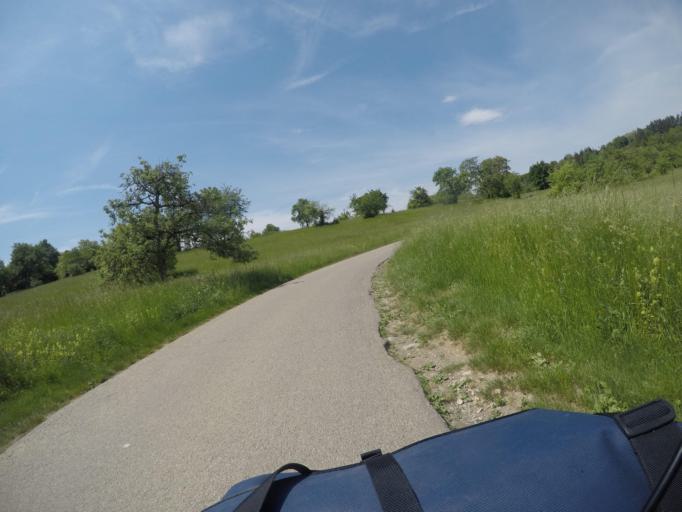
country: DE
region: Baden-Wuerttemberg
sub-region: Karlsruhe Region
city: Konigsbach-Stein
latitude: 48.9363
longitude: 8.6200
